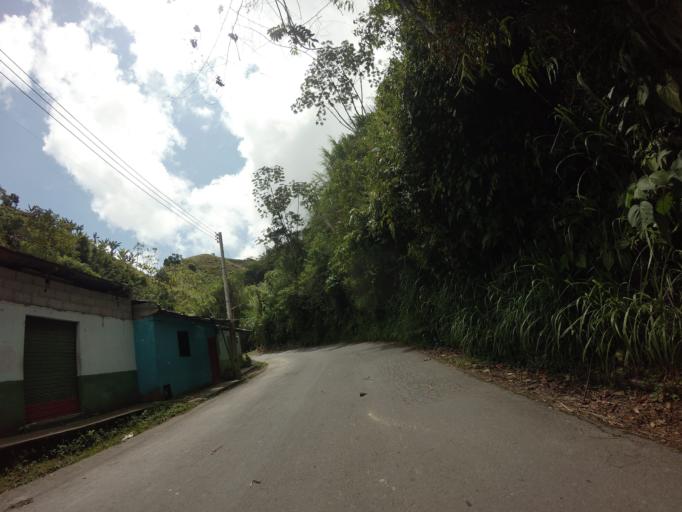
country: CO
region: Caldas
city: Marquetalia
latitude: 5.2987
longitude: -75.0596
